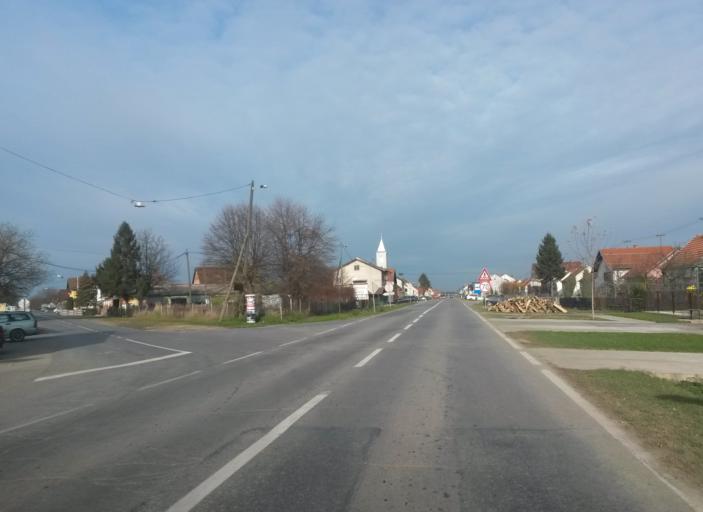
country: HR
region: Osjecko-Baranjska
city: Viskovci
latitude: 45.3491
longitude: 18.4228
